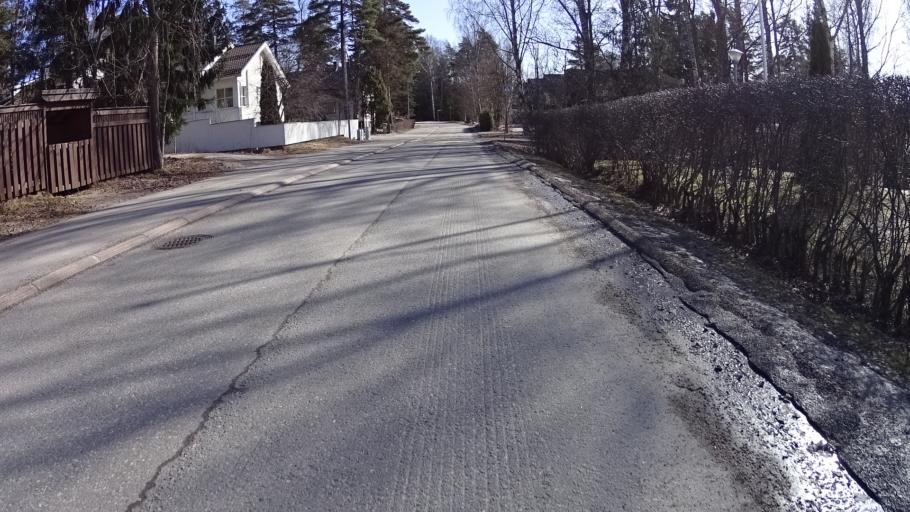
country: FI
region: Uusimaa
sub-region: Helsinki
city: Otaniemi
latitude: 60.2021
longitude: 24.8069
